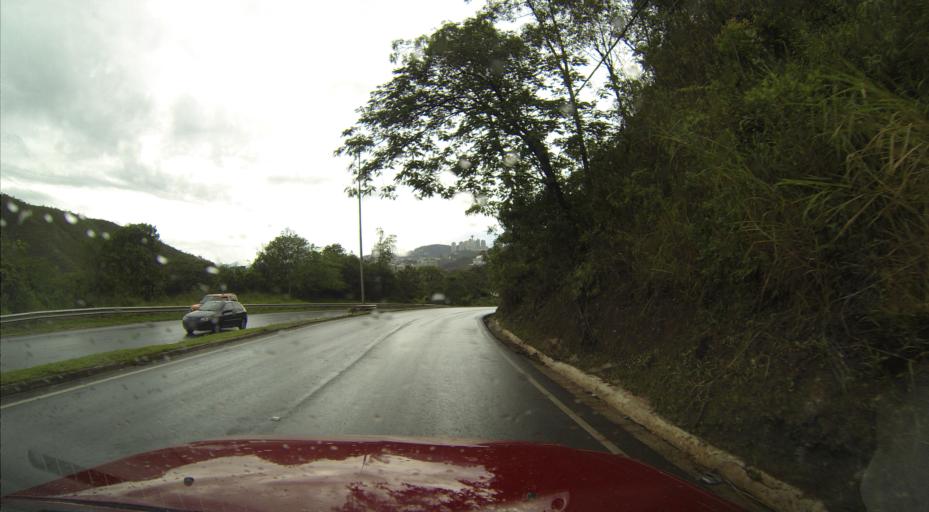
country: BR
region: Minas Gerais
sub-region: Nova Lima
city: Nova Lima
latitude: -19.9967
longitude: -43.9164
